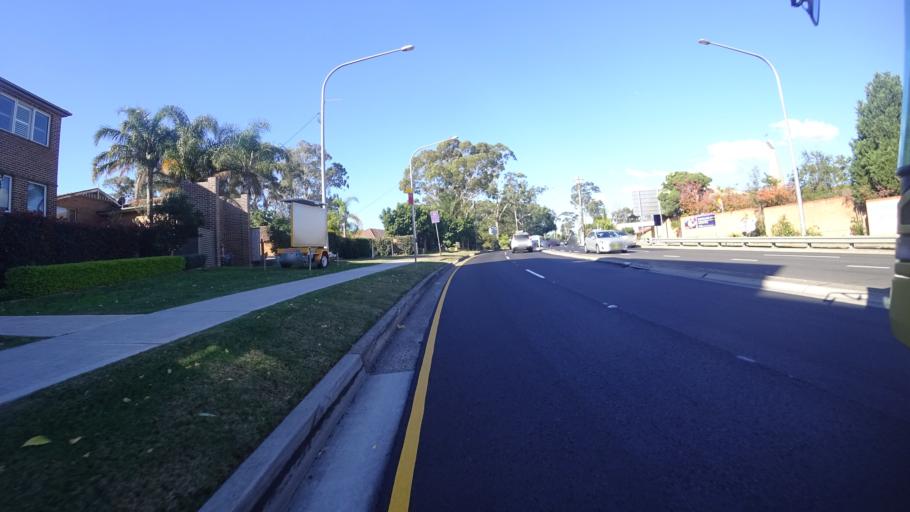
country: AU
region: New South Wales
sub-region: The Hills Shire
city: Castle Hill
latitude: -33.7311
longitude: 151.0115
